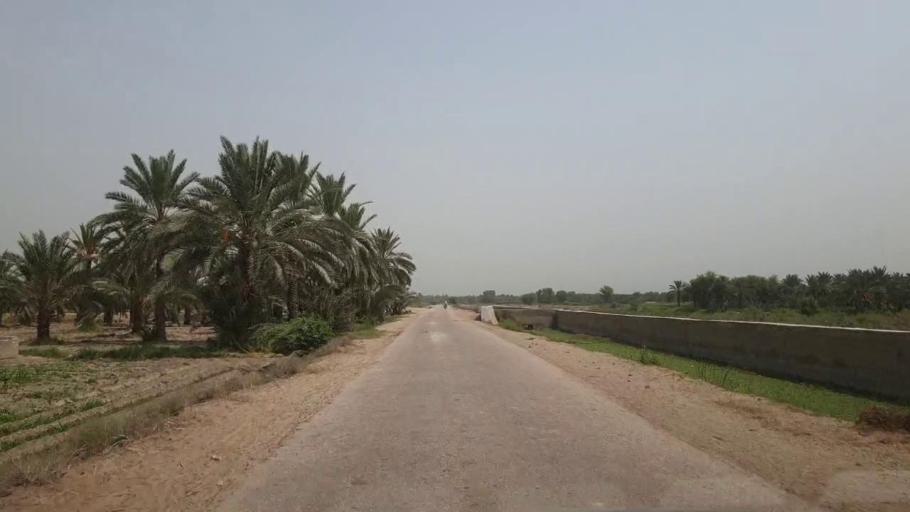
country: PK
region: Sindh
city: Gambat
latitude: 27.4263
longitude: 68.5599
